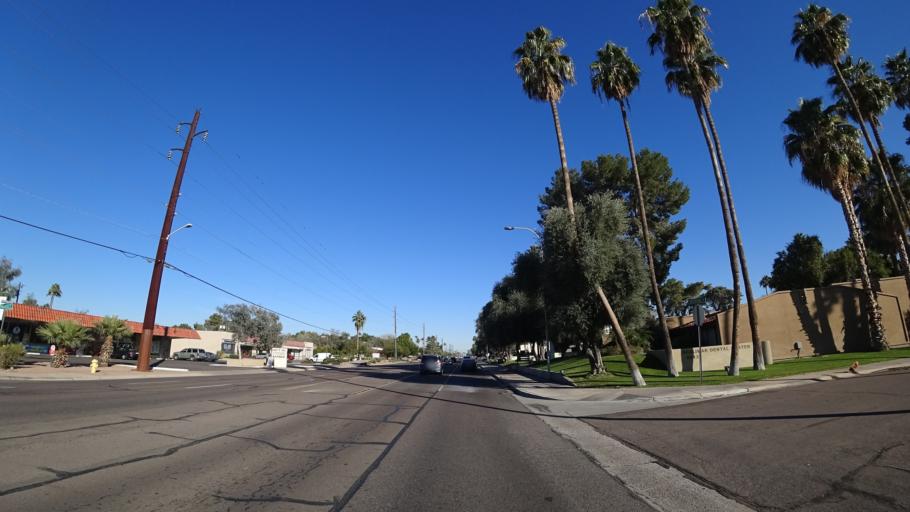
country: US
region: Arizona
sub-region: Maricopa County
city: Tempe
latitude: 33.3929
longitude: -111.8990
